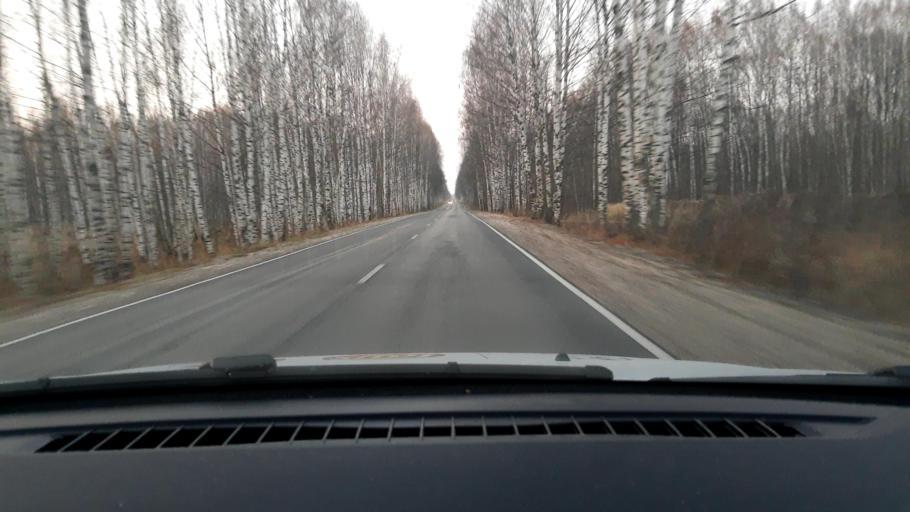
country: RU
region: Nizjnij Novgorod
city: Neklyudovo
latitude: 56.4874
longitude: 43.8640
